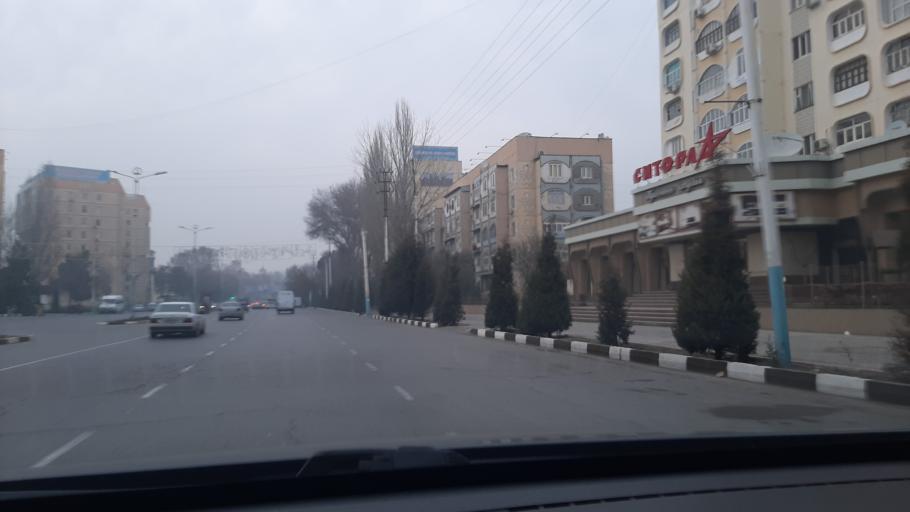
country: TJ
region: Viloyati Sughd
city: Khujand
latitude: 40.2668
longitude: 69.6522
